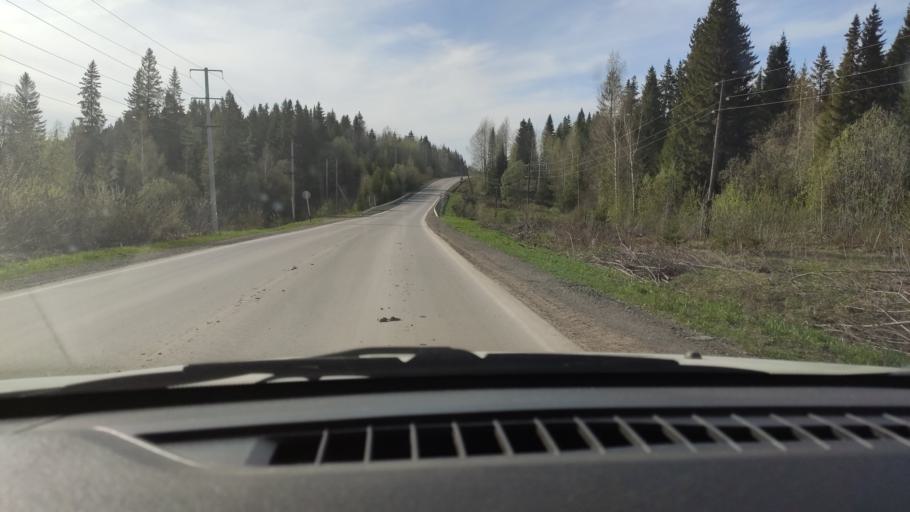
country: RU
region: Perm
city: Novyye Lyady
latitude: 57.9252
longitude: 56.6536
